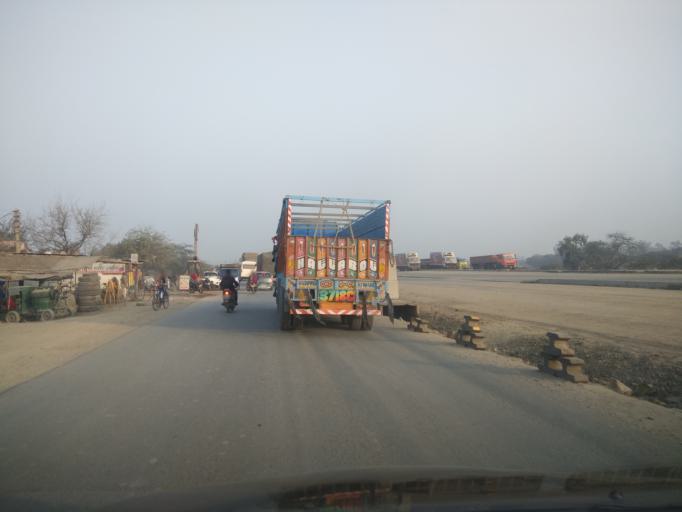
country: IN
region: Uttar Pradesh
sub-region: Varanasi
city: Ramnagar
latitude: 25.2522
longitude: 83.0646
